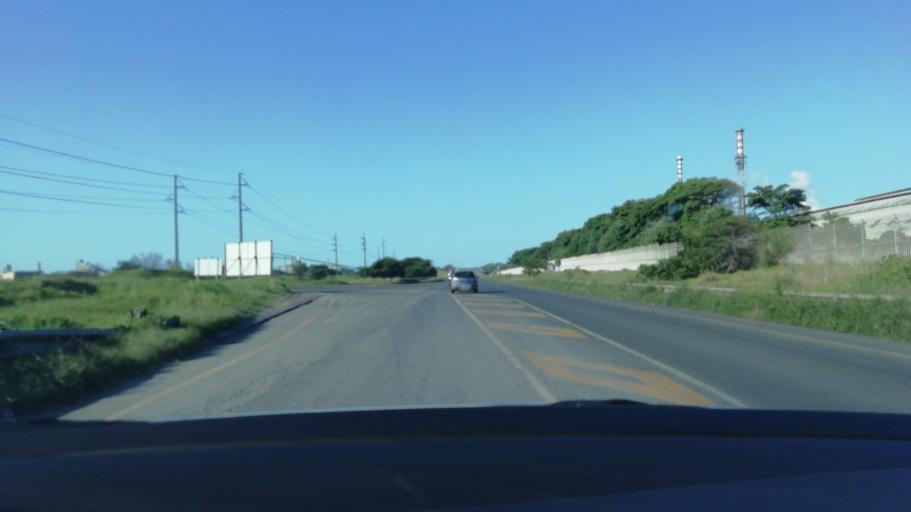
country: ZA
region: KwaZulu-Natal
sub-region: uThungulu District Municipality
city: Richards Bay
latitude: -28.7756
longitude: 32.0314
